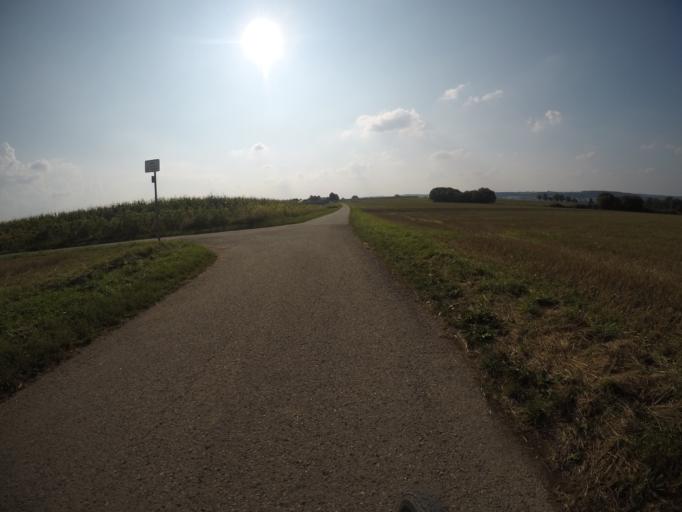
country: DE
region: Baden-Wuerttemberg
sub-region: Tuebingen Region
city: Pliezhausen
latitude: 48.5483
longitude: 9.2381
